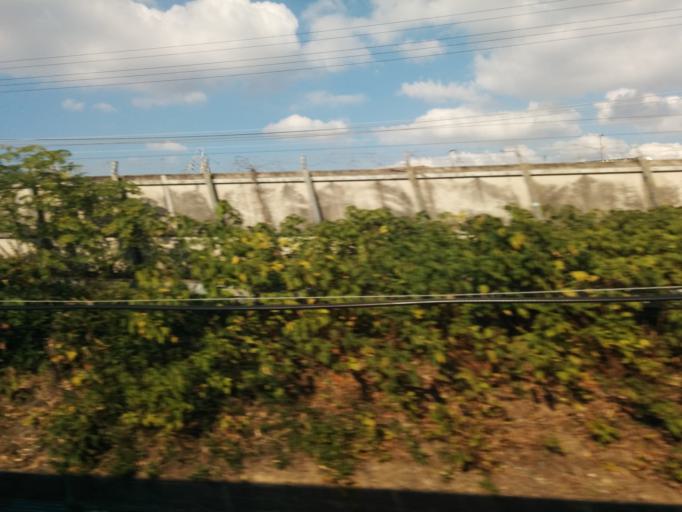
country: JP
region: Aichi
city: Toyohashi
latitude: 34.7292
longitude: 137.4238
